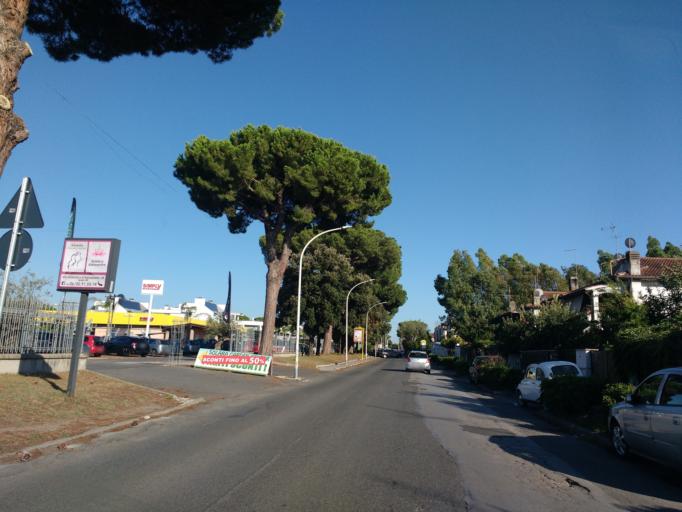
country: IT
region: Latium
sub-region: Citta metropolitana di Roma Capitale
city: Acilia-Castel Fusano-Ostia Antica
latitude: 41.7587
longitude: 12.3645
